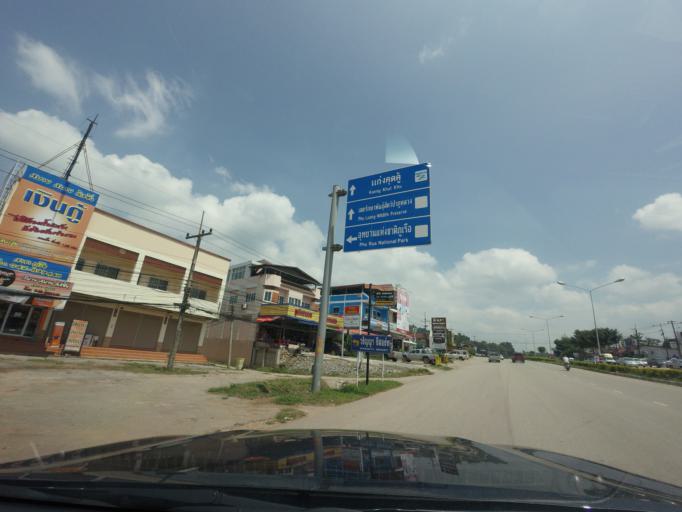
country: TH
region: Loei
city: Phu Ruea
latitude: 17.4529
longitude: 101.3618
